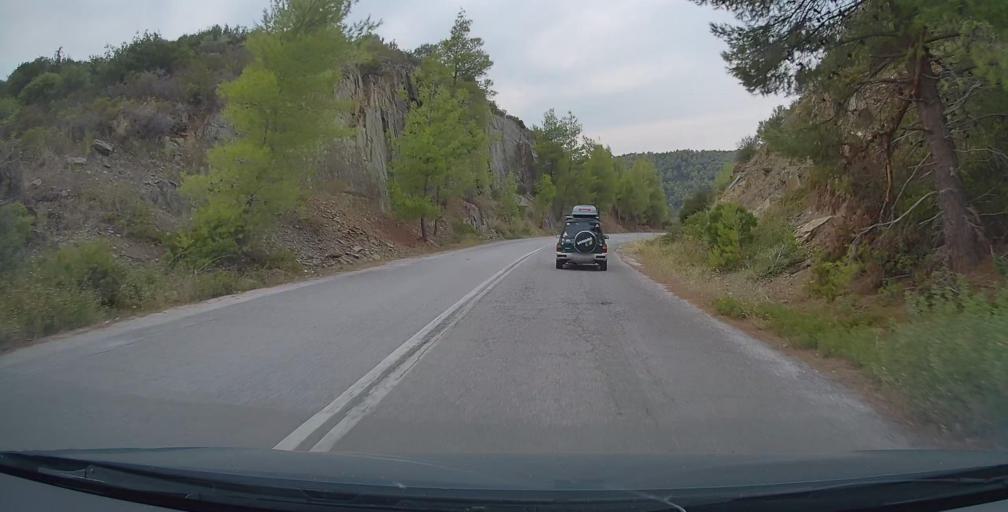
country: GR
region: Central Macedonia
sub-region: Nomos Chalkidikis
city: Sykia
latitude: 40.0212
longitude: 23.8629
